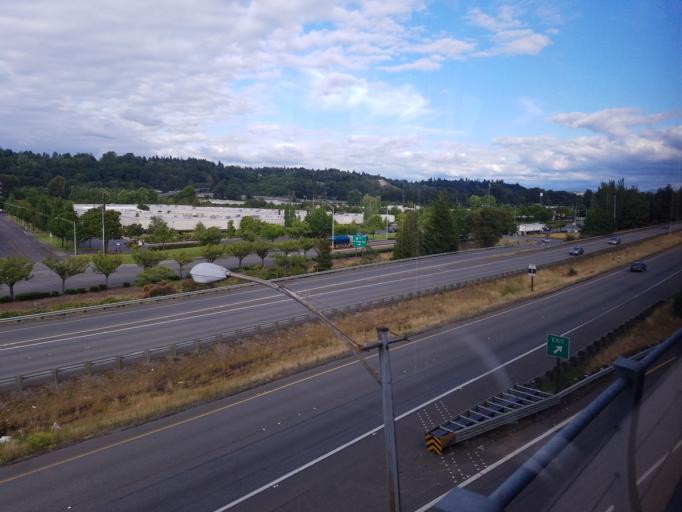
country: US
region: Washington
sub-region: King County
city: Riverton
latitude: 47.4873
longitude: -122.2785
